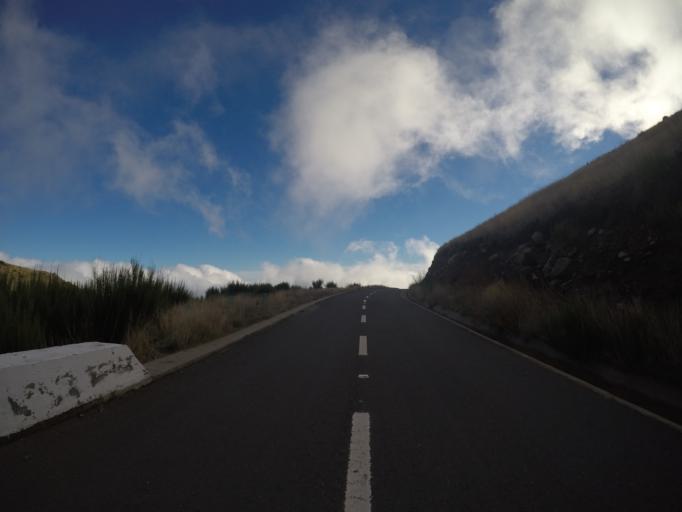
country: PT
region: Madeira
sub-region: Camara de Lobos
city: Curral das Freiras
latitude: 32.7159
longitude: -16.9539
